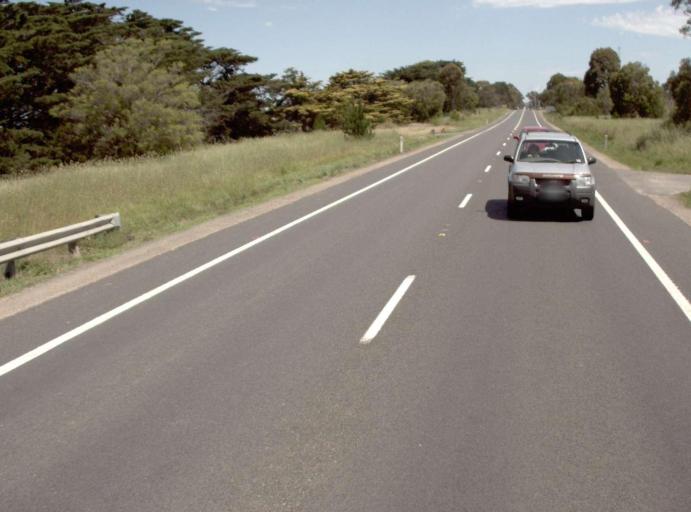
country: AU
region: Victoria
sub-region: Wellington
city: Sale
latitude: -38.0745
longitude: 147.0727
